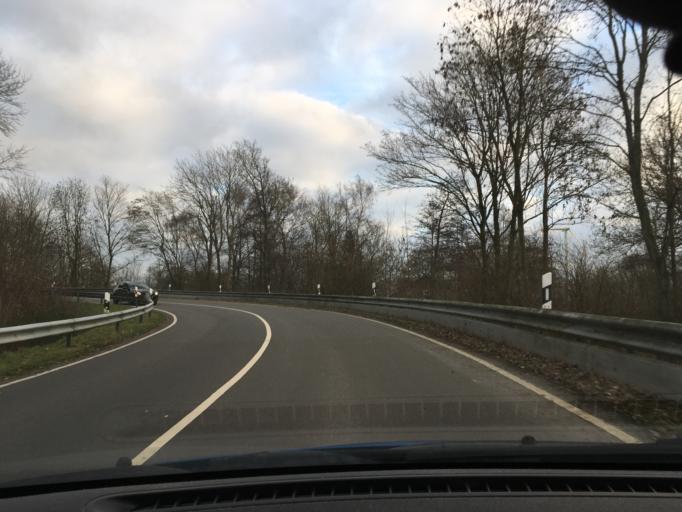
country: DE
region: Schleswig-Holstein
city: Hemme
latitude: 54.2753
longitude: 9.0075
